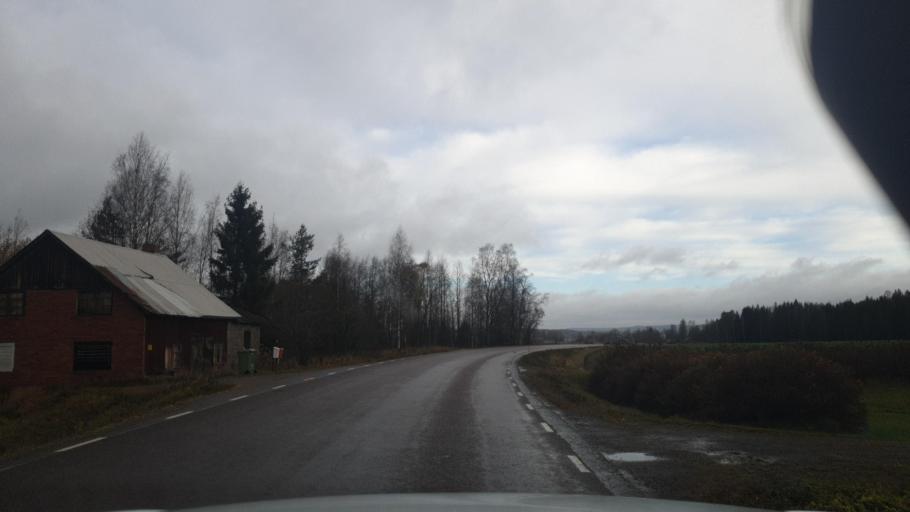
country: SE
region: Vaermland
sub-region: Eda Kommun
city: Charlottenberg
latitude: 59.7584
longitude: 12.1577
